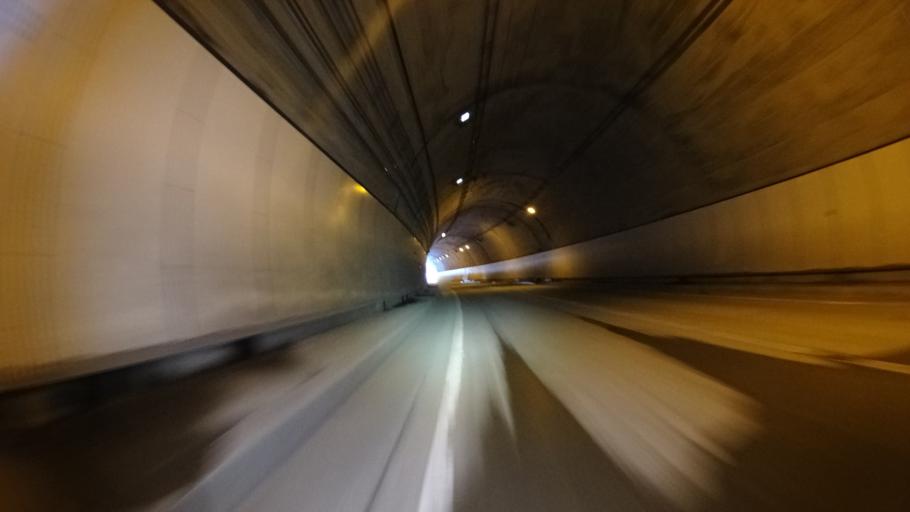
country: JP
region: Yamanashi
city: Uenohara
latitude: 35.6979
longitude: 139.1026
